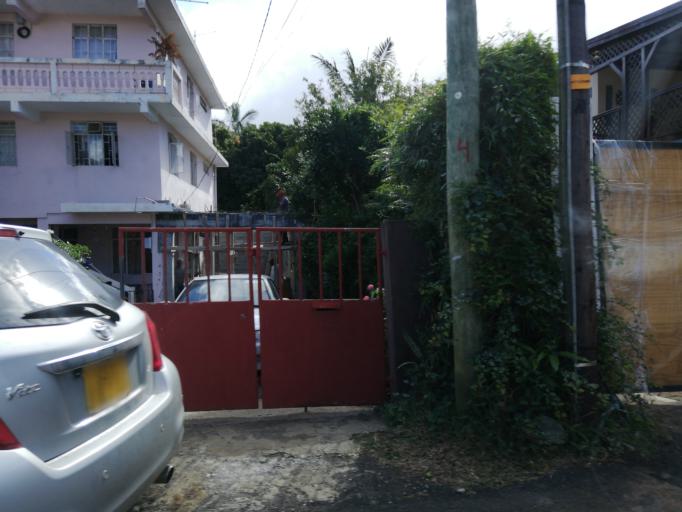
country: MU
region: Moka
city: Moka
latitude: -20.2253
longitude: 57.4728
